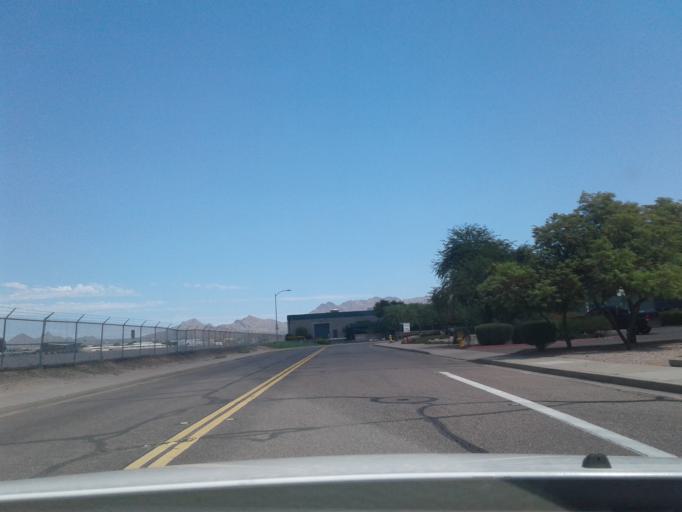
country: US
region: Arizona
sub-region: Maricopa County
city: Paradise Valley
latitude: 33.6171
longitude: -111.9154
